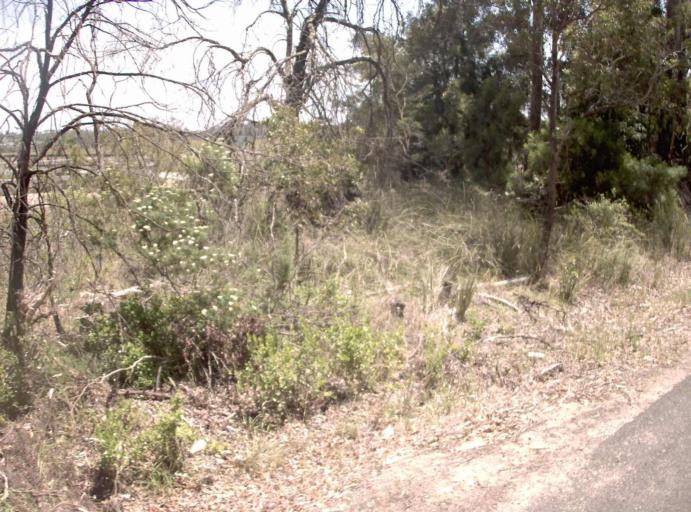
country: AU
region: Victoria
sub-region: East Gippsland
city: Lakes Entrance
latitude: -37.8408
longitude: 148.0358
